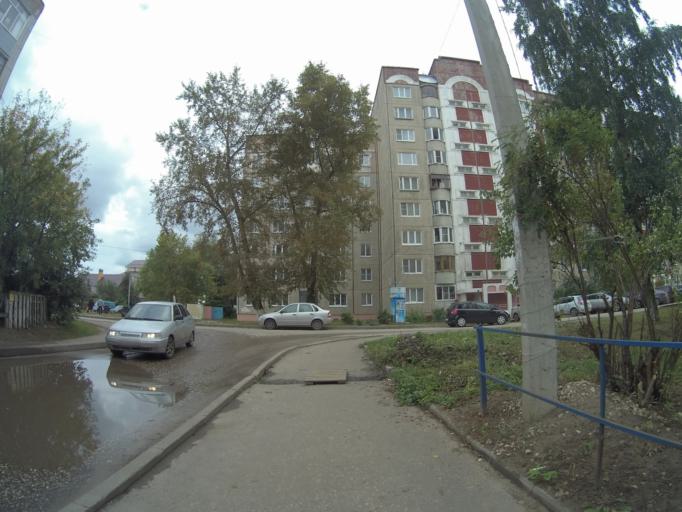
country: RU
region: Vladimir
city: Vladimir
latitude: 56.1168
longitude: 40.3543
